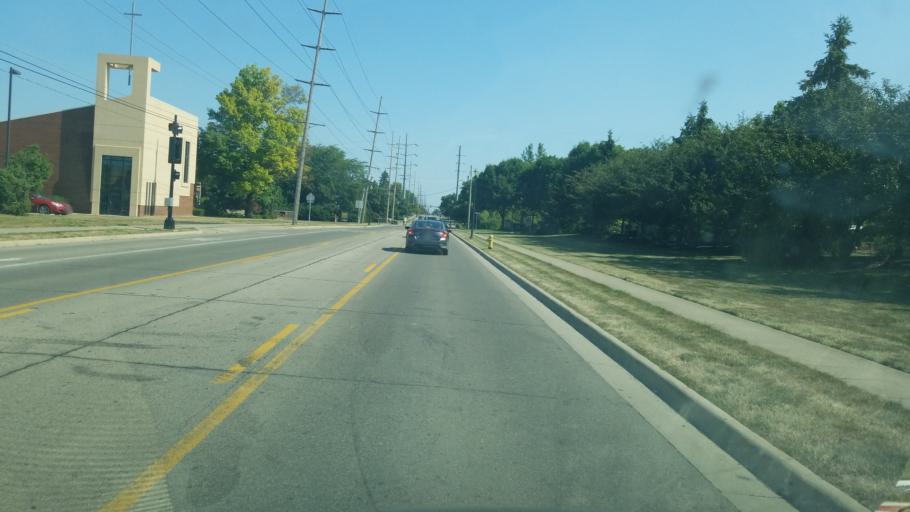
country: US
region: Ohio
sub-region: Franklin County
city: Grove City
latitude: 39.8703
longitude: -83.0703
